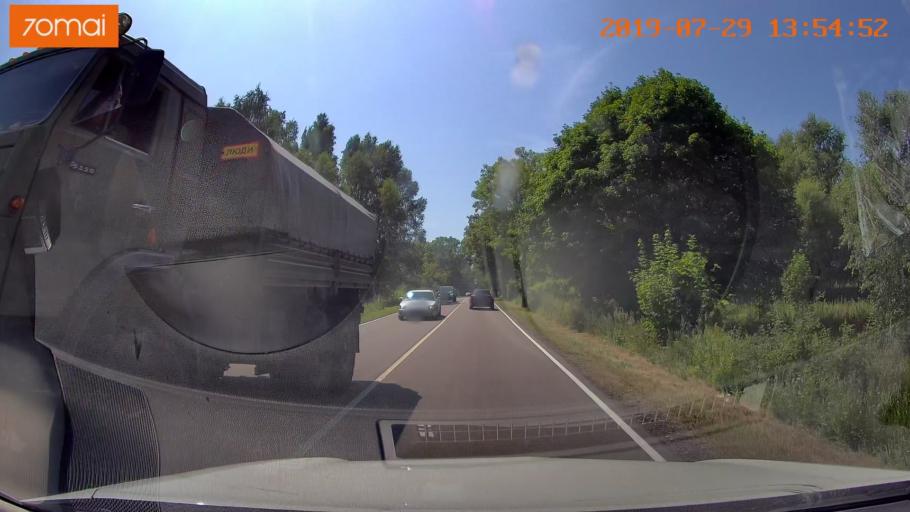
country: RU
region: Kaliningrad
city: Primorsk
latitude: 54.7197
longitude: 19.9623
